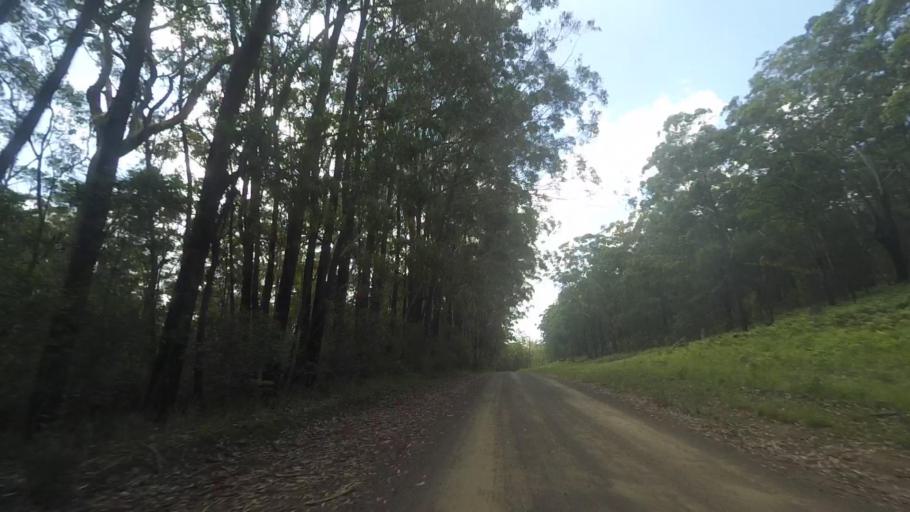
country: AU
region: New South Wales
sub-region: Great Lakes
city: Bulahdelah
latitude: -32.4997
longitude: 152.2806
